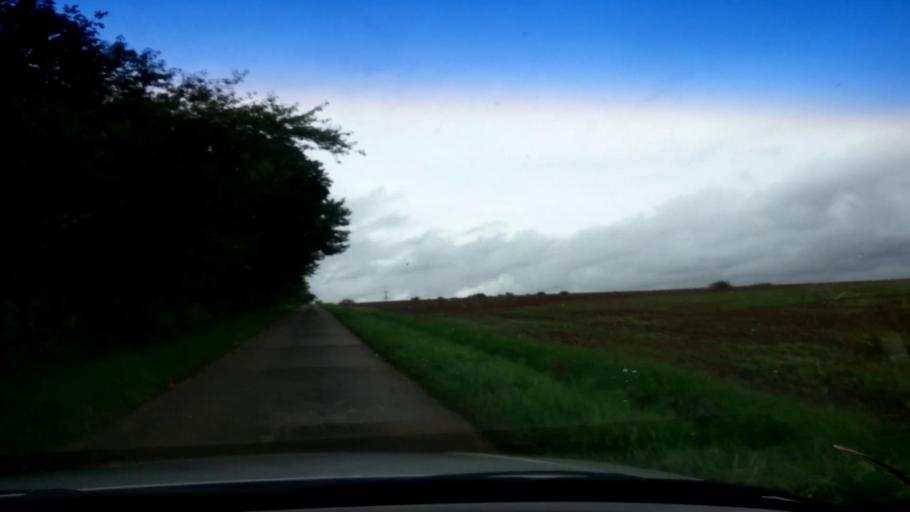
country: DE
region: Bavaria
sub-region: Upper Franconia
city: Memmelsdorf
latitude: 49.9513
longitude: 10.9801
